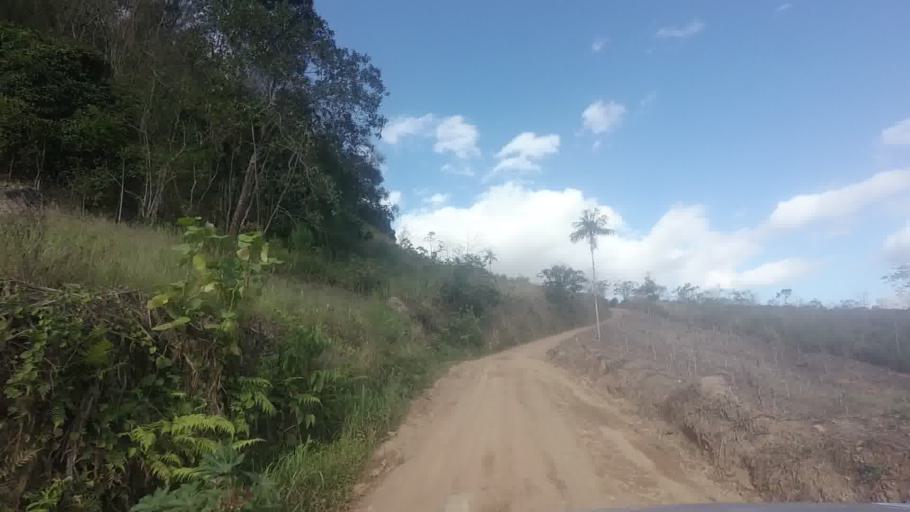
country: BR
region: Espirito Santo
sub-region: Sao Jose Do Calcado
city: Sao Jose do Calcado
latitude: -20.9856
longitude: -41.5171
